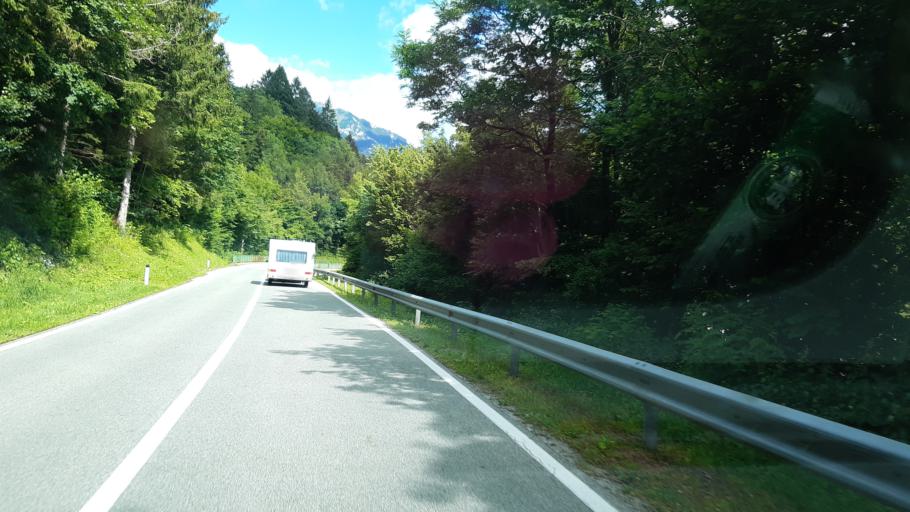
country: SI
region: Trzic
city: Trzic
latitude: 46.3704
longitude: 14.3038
